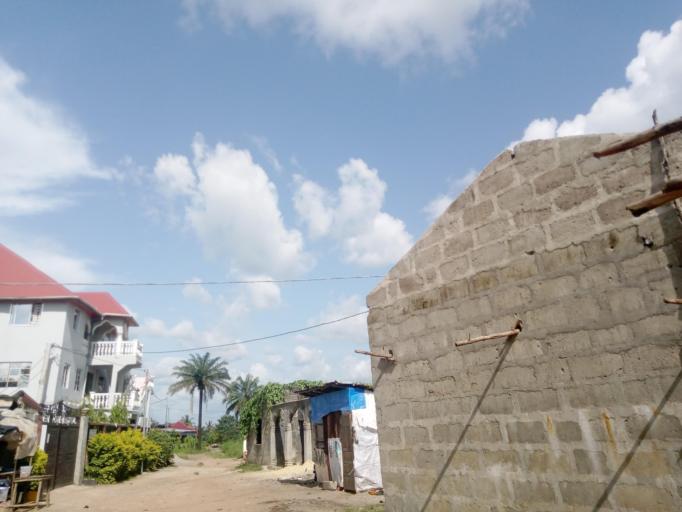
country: SL
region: Northern Province
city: Makeni
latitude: 8.9082
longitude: -12.0299
